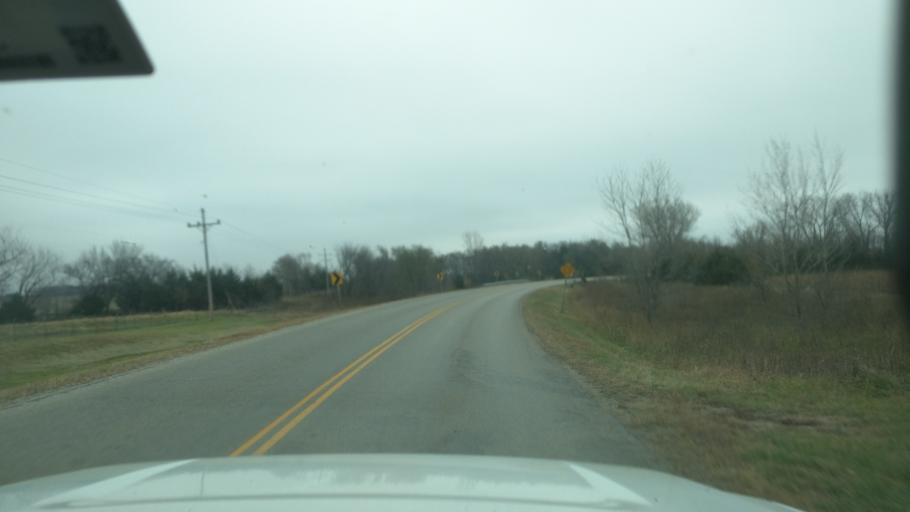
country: US
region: Kansas
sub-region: Lyon County
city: Emporia
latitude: 38.4982
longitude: -96.2543
